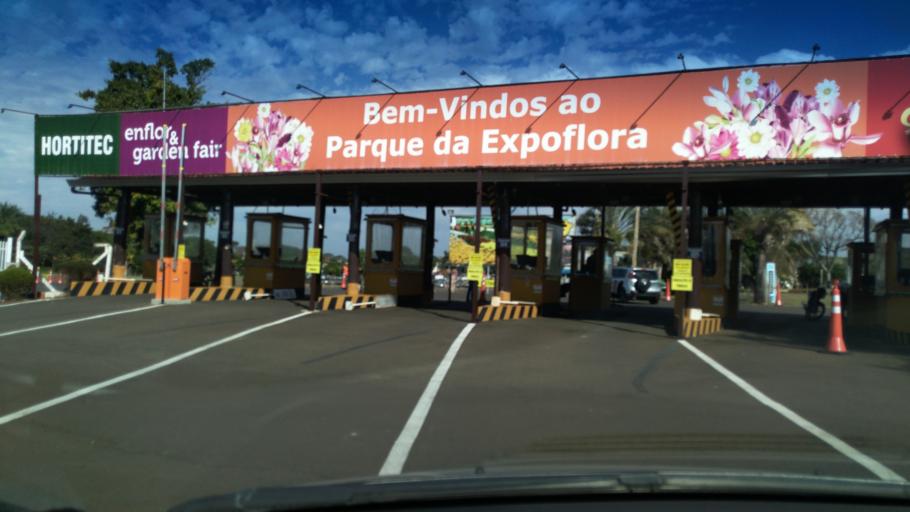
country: BR
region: Sao Paulo
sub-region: Jaguariuna
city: Jaguariuna
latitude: -22.6237
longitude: -47.0581
